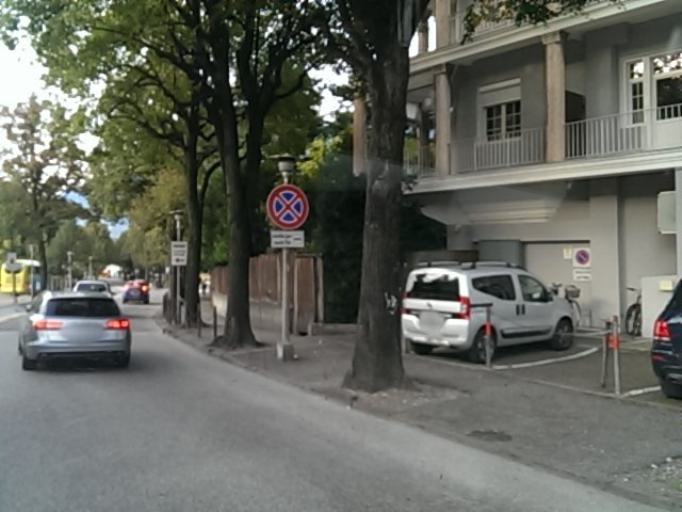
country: IT
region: Trentino-Alto Adige
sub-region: Bolzano
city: Merano
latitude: 46.6695
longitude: 11.1595
